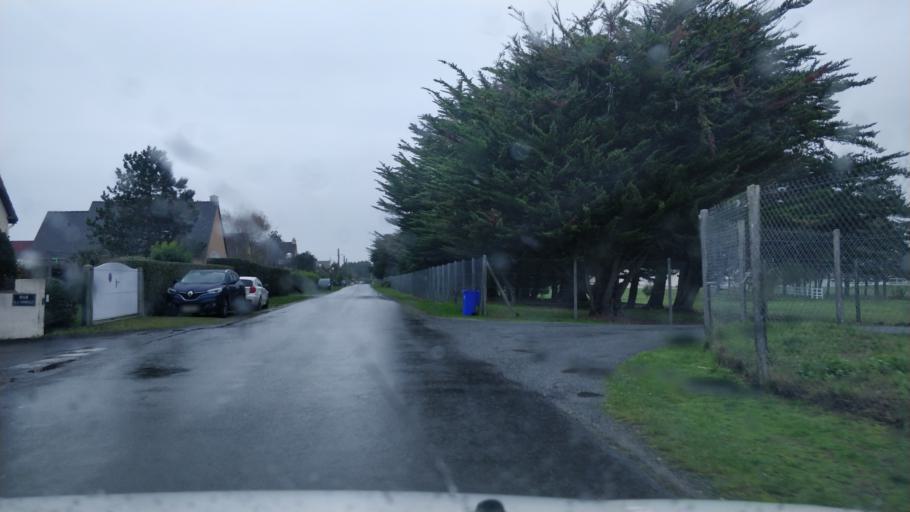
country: FR
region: Lower Normandy
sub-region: Departement de la Manche
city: Brehal
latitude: 48.8992
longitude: -1.5653
